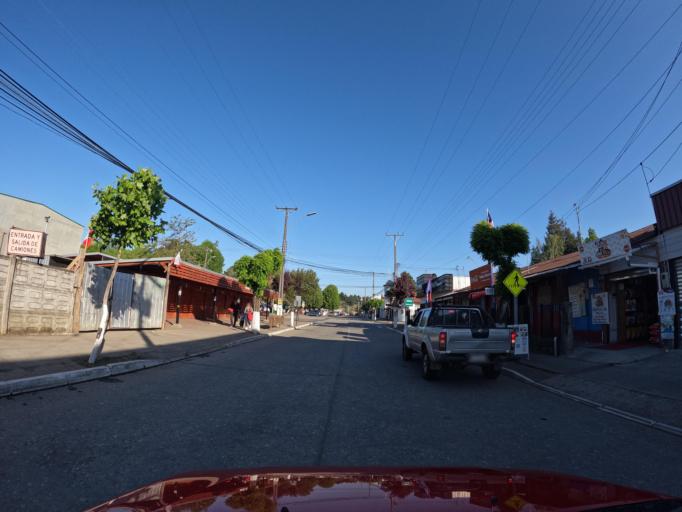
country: CL
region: Biobio
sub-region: Provincia de Concepcion
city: Lota
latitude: -37.1749
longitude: -72.9392
